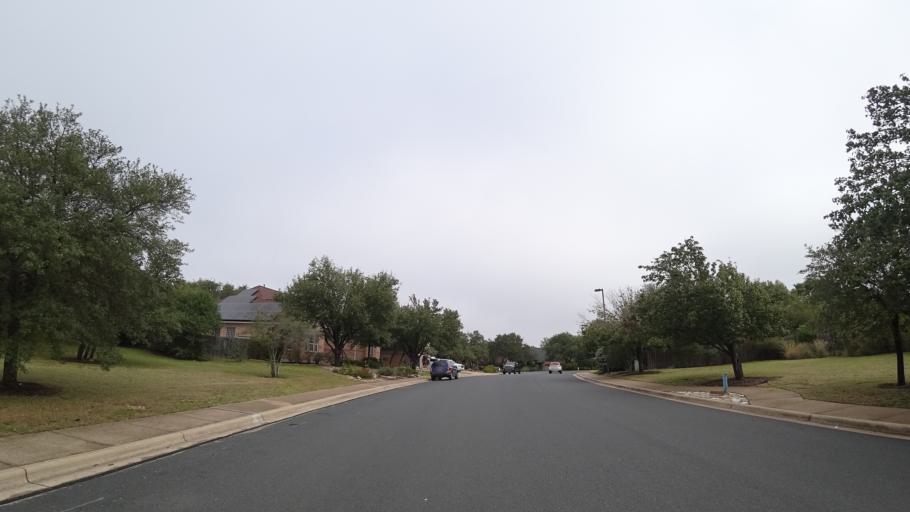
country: US
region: Texas
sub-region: Travis County
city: Shady Hollow
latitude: 30.1927
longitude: -97.8768
